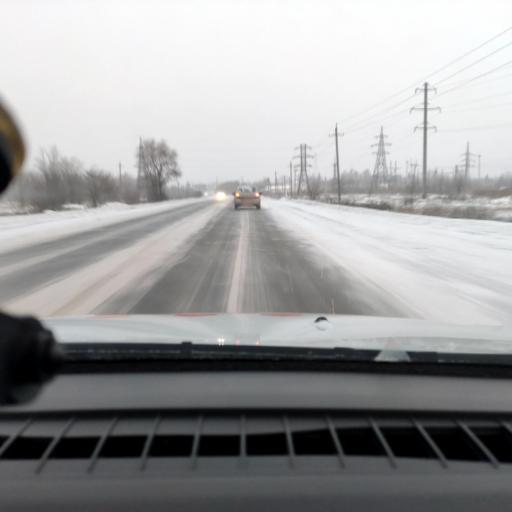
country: RU
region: Samara
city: Otradnyy
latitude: 53.3484
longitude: 51.3164
